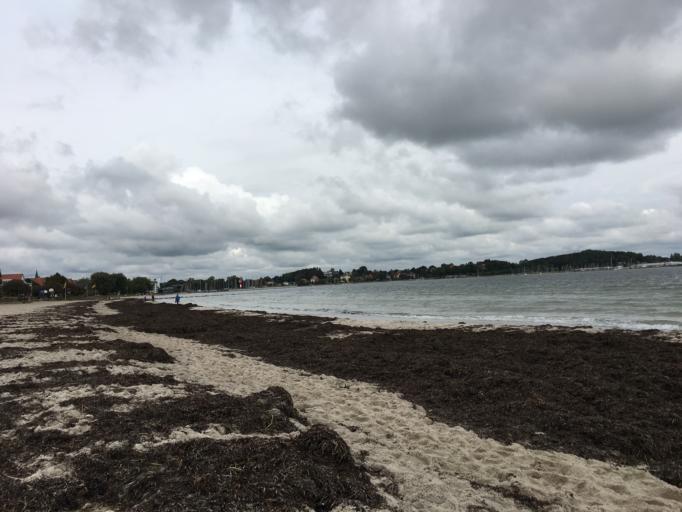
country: DE
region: Schleswig-Holstein
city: Eckernforde
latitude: 54.4671
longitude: 9.8406
